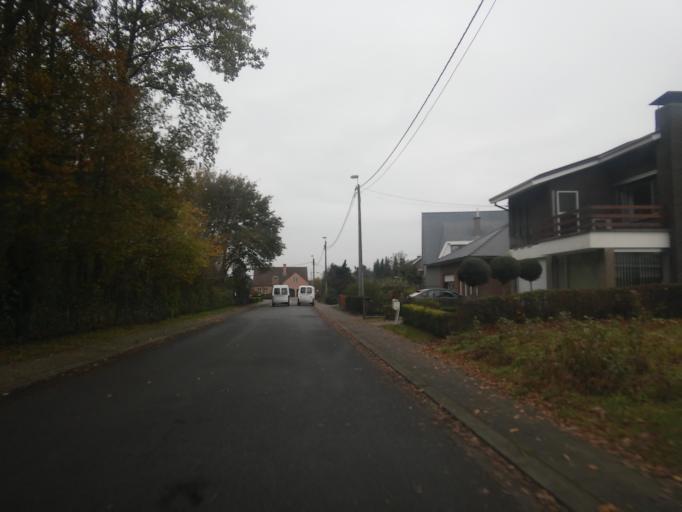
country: BE
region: Flanders
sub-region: Provincie Antwerpen
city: Bornem
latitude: 51.0908
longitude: 4.2476
